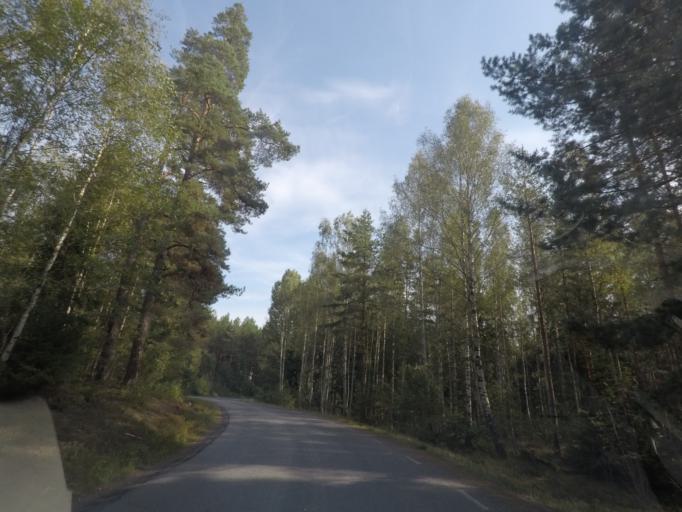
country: SE
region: Vaestmanland
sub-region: Kungsors Kommun
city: Kungsoer
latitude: 59.5094
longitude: 16.1539
